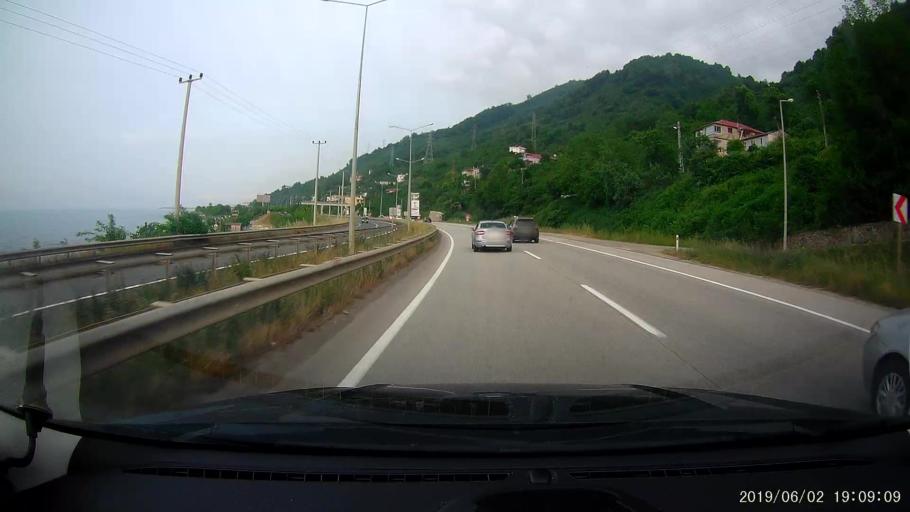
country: TR
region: Ordu
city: Gulyali
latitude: 40.9743
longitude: 38.0229
